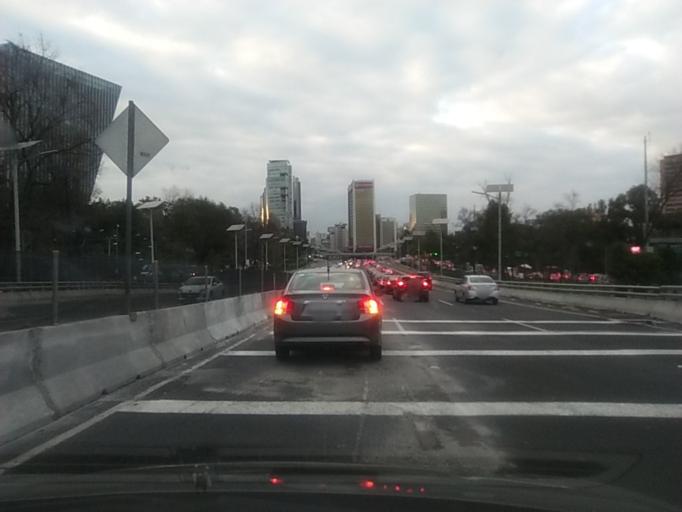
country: MX
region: Mexico City
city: Polanco
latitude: 19.4235
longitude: -99.1995
